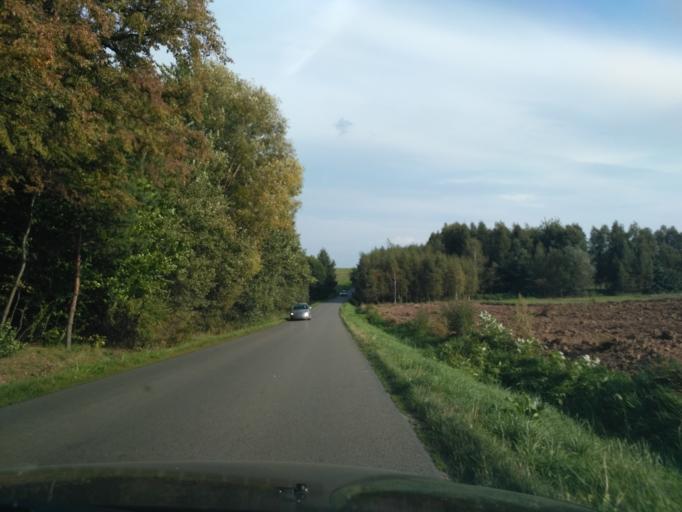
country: PL
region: Subcarpathian Voivodeship
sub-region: Powiat rzeszowski
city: Zglobien
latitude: 50.0046
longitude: 21.8660
